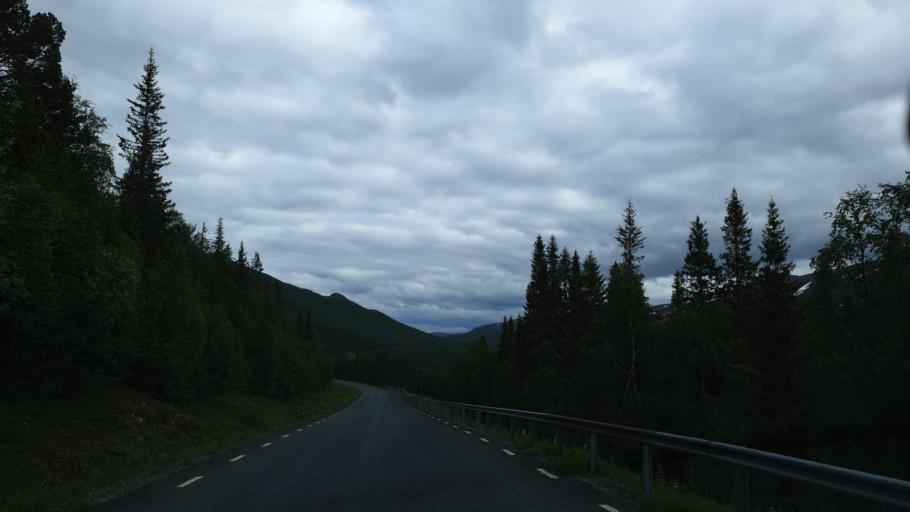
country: NO
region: Nordland
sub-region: Hattfjelldal
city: Hattfjelldal
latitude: 65.4418
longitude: 14.5484
